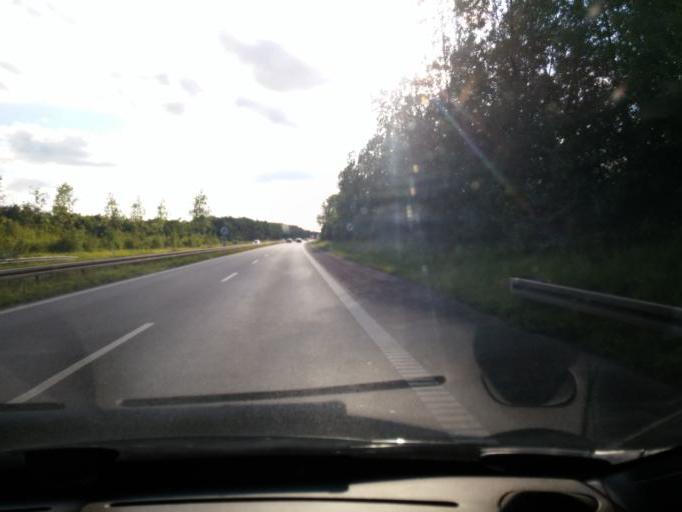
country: DK
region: South Denmark
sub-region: Nyborg Kommune
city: Nyborg
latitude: 55.3319
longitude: 10.7410
